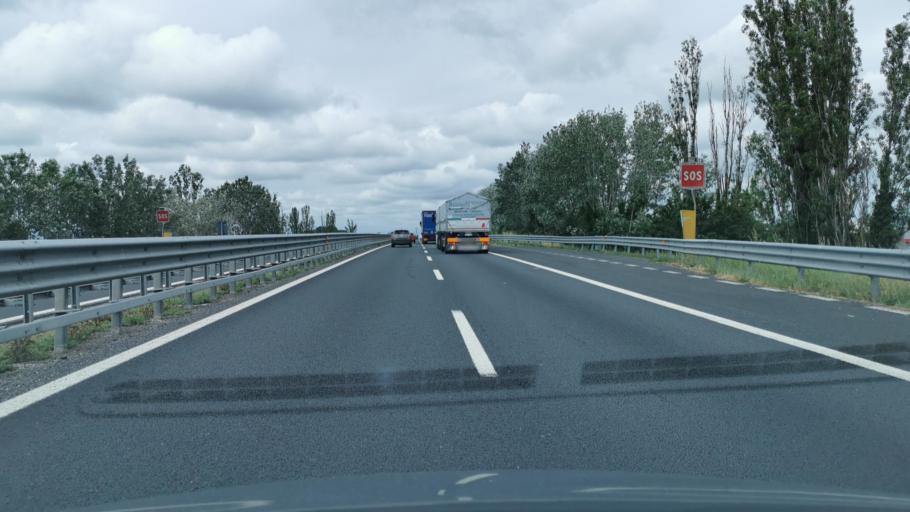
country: IT
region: Emilia-Romagna
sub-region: Provincia di Ravenna
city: Bagnacavallo
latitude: 44.4057
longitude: 11.9915
